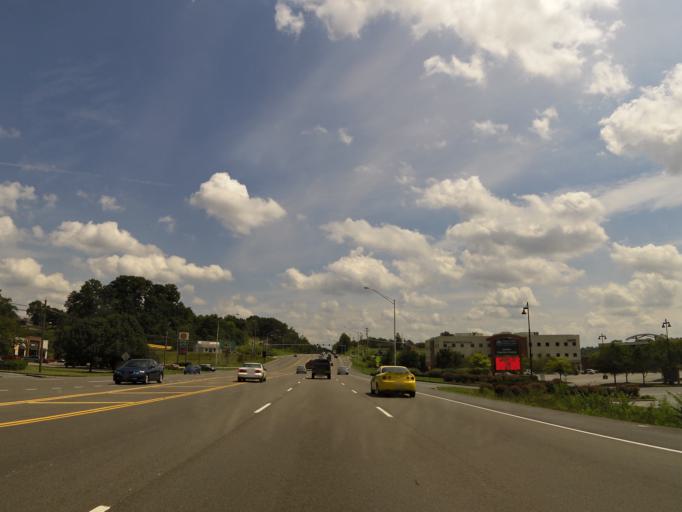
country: US
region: Tennessee
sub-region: Sullivan County
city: Kingsport
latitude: 36.5593
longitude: -82.5536
